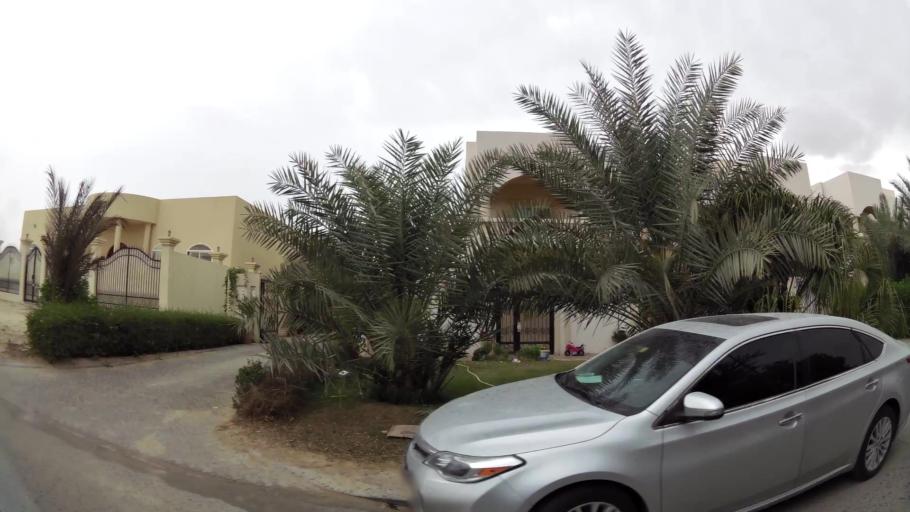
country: AE
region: Abu Dhabi
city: Abu Dhabi
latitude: 24.3684
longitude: 54.6476
